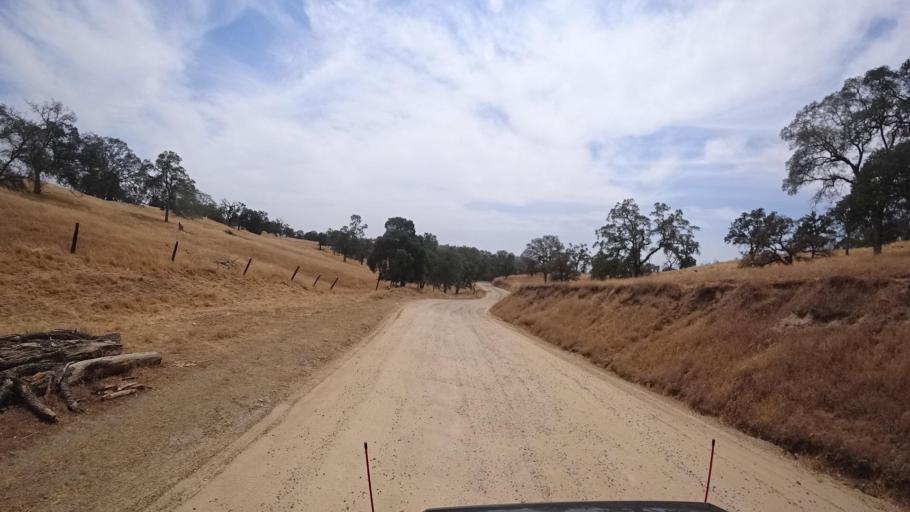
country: US
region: California
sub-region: Madera County
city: Ahwahnee
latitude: 37.3634
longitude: -119.8682
